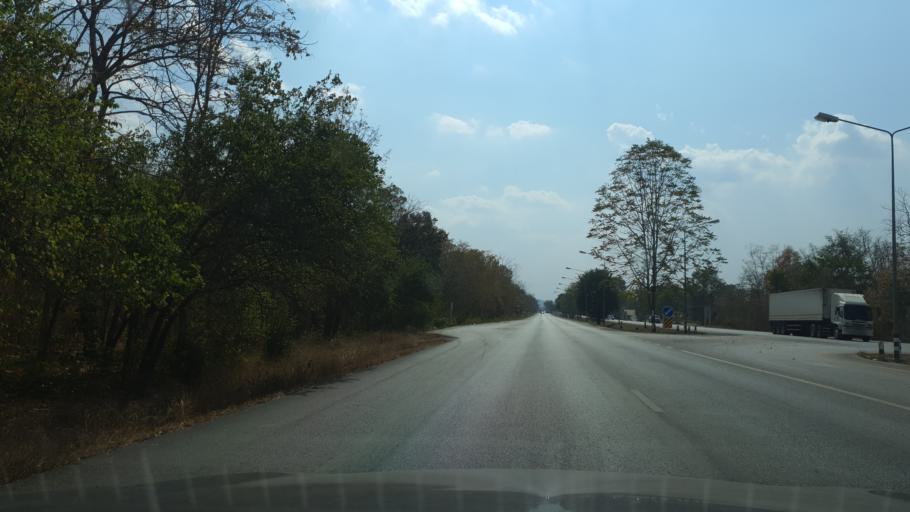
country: TH
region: Lampang
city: Mae Phrik
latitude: 17.4406
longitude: 99.1590
